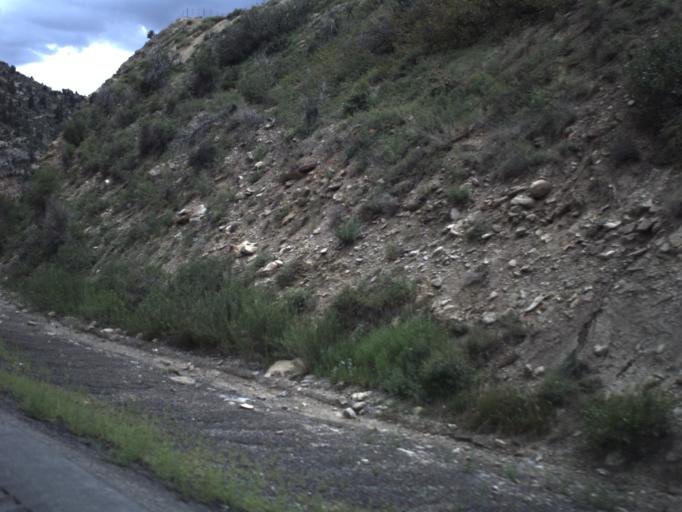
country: US
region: Utah
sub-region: Carbon County
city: Helper
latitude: 39.8000
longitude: -110.9330
